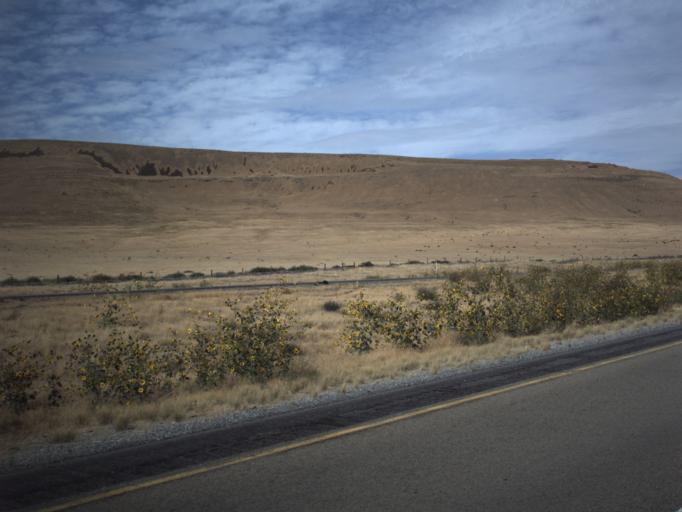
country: US
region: Utah
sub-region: Tooele County
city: Grantsville
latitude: 40.8124
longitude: -112.8716
